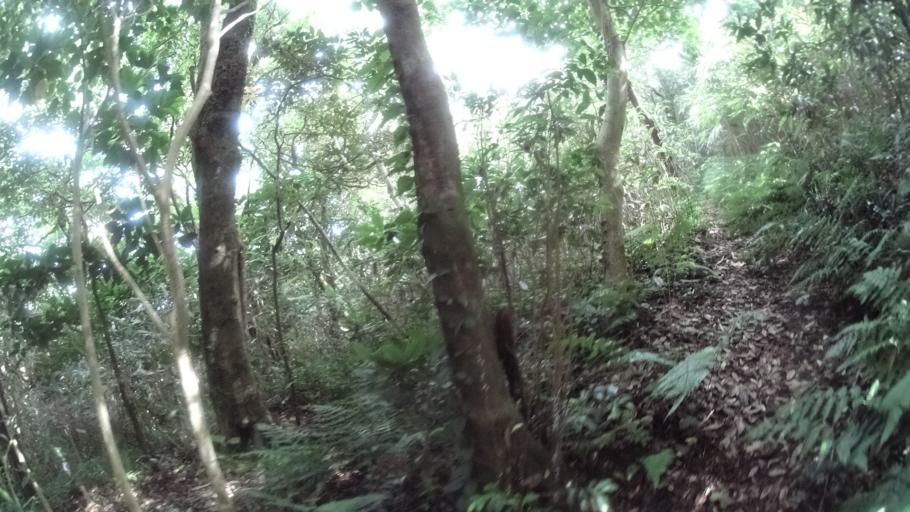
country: JP
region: Shizuoka
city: Shimoda
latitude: 34.5195
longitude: 139.2761
